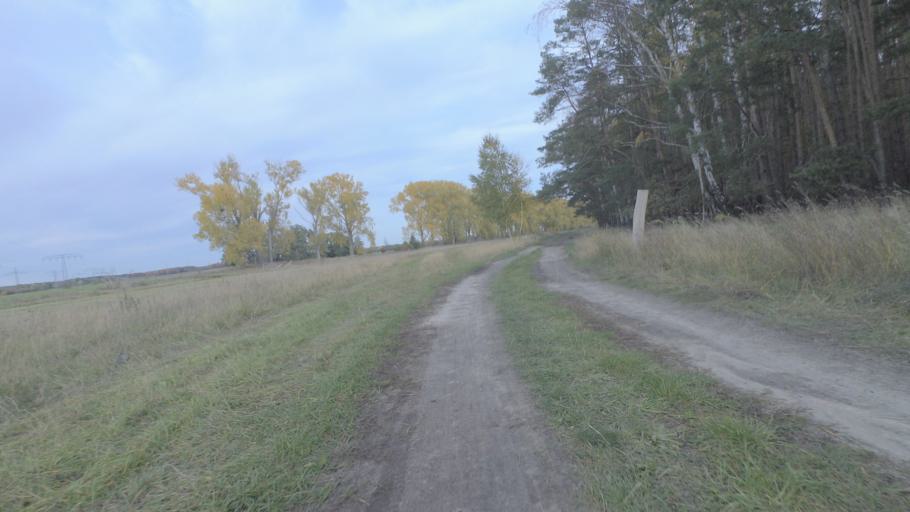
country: DE
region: Brandenburg
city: Ludwigsfelde
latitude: 52.2535
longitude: 13.2736
